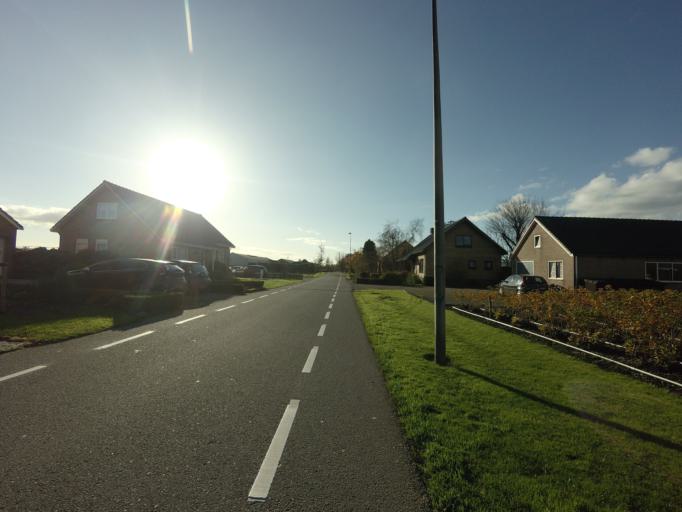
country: NL
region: South Holland
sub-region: Gemeente Nieuwkoop
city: Nieuwkoop
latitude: 52.1900
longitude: 4.7288
